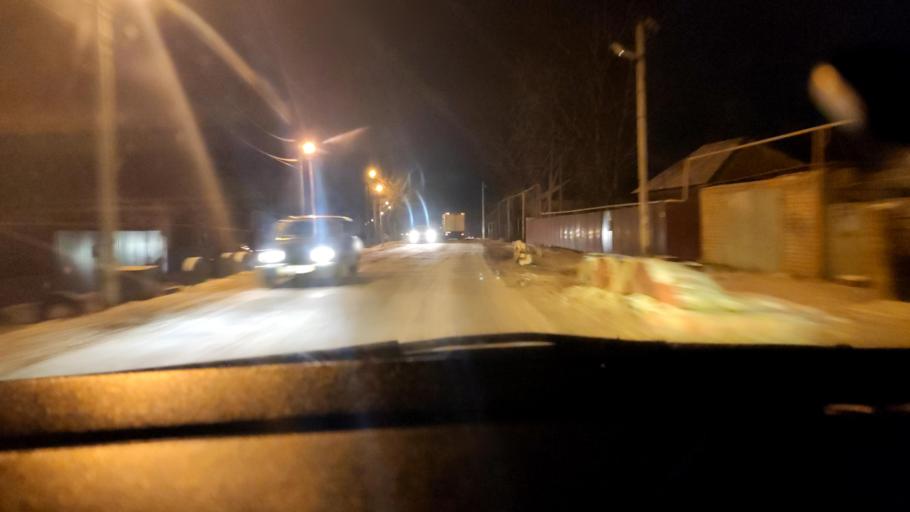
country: RU
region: Voronezj
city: Pridonskoy
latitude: 51.6673
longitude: 39.0819
